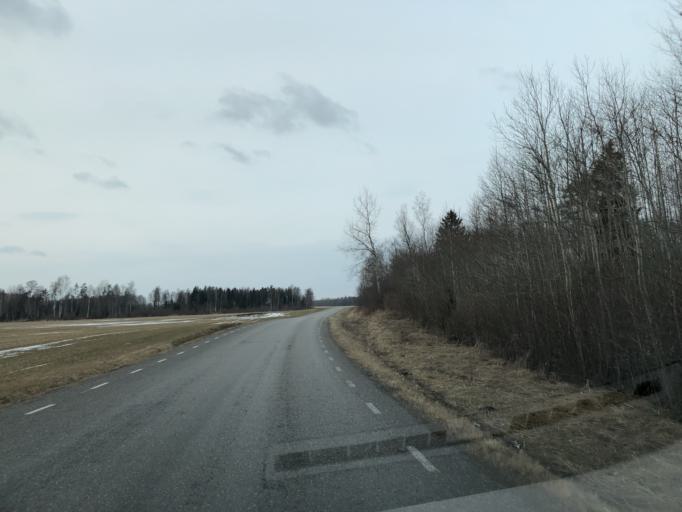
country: EE
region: Paernumaa
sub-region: Vaendra vald (alev)
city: Vandra
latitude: 58.6716
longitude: 25.0123
